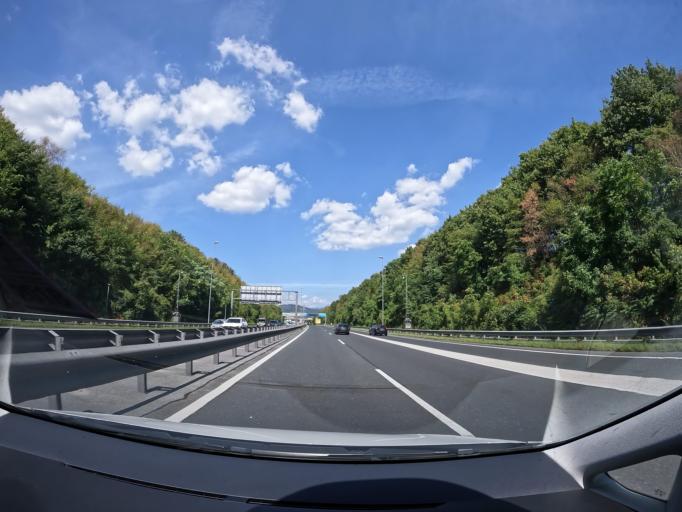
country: SI
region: Medvode
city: Zgornje Pirnice
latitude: 46.1044
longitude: 14.4550
